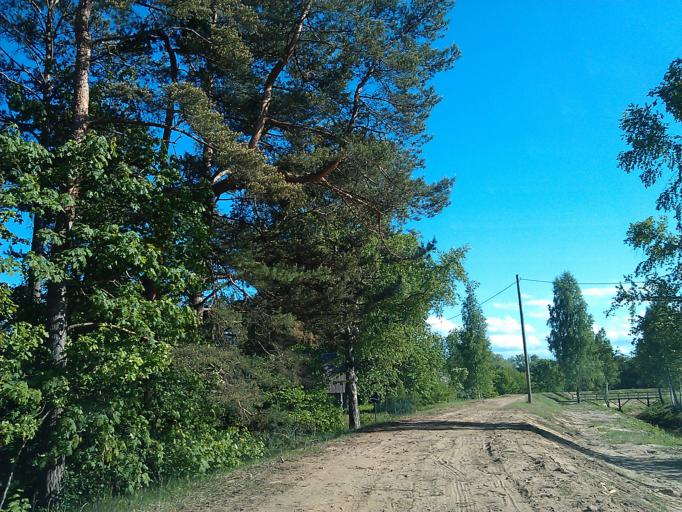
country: LV
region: Adazi
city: Adazi
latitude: 57.0974
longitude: 24.3298
